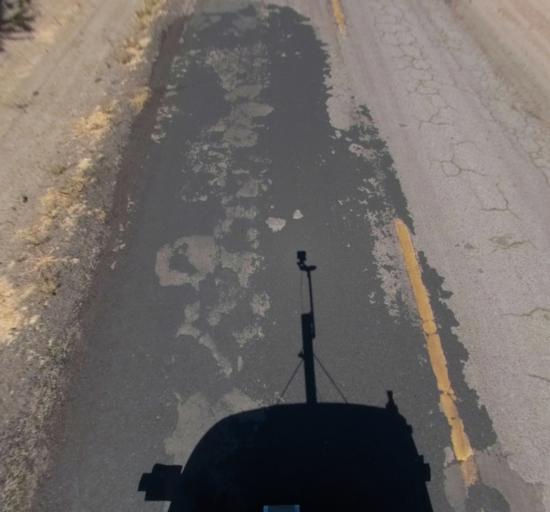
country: US
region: California
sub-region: Madera County
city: Parkwood
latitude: 36.8802
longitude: -120.0978
